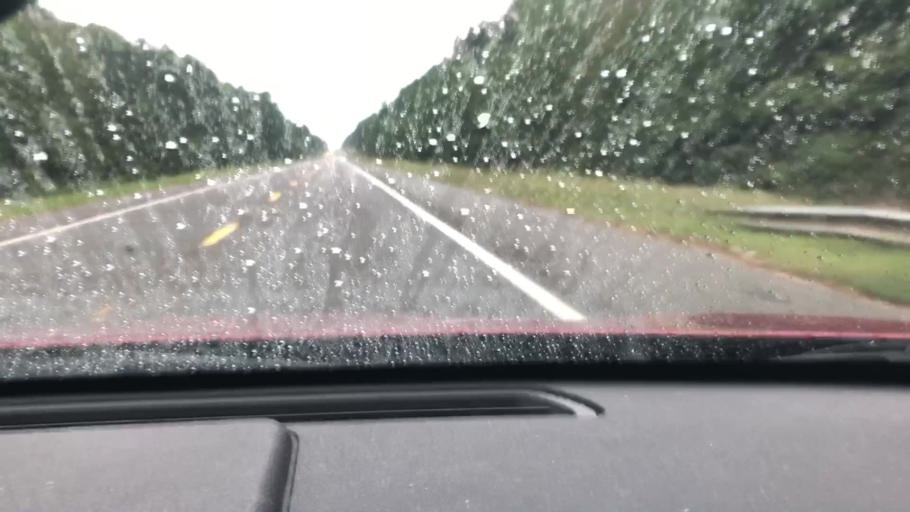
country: US
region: Arkansas
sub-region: Columbia County
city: Magnolia
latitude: 33.3039
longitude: -93.2712
